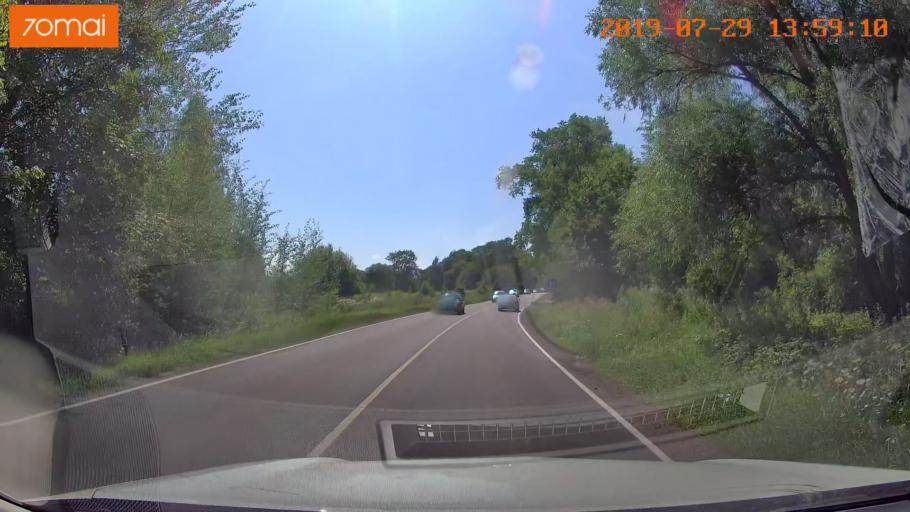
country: RU
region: Kaliningrad
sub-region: Gorod Kaliningrad
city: Baltiysk
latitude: 54.6868
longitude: 19.9338
